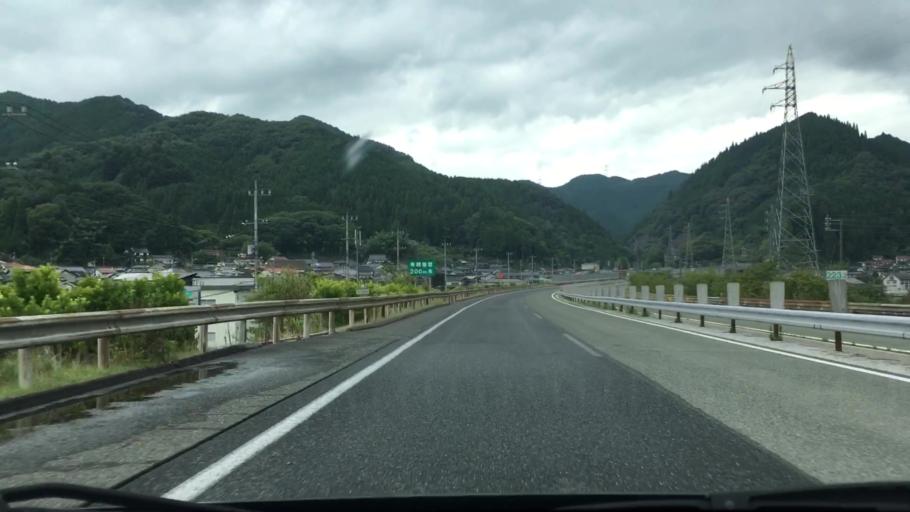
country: JP
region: Okayama
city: Niimi
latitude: 35.0078
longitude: 133.4374
